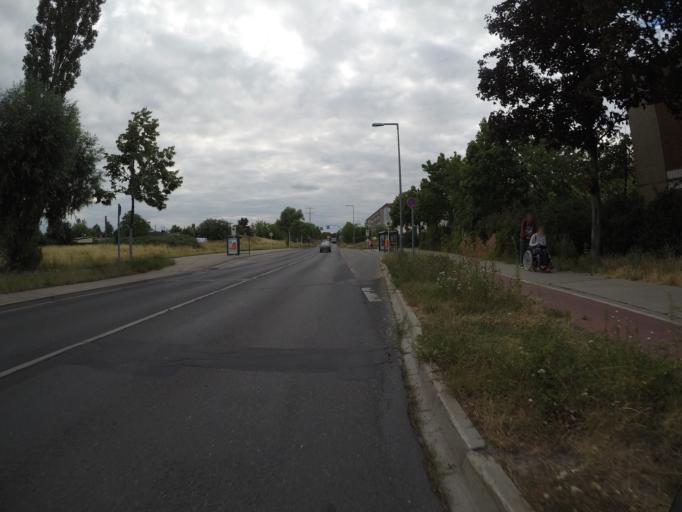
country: DE
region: Berlin
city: Kaulsdorf
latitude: 52.5188
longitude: 13.6011
